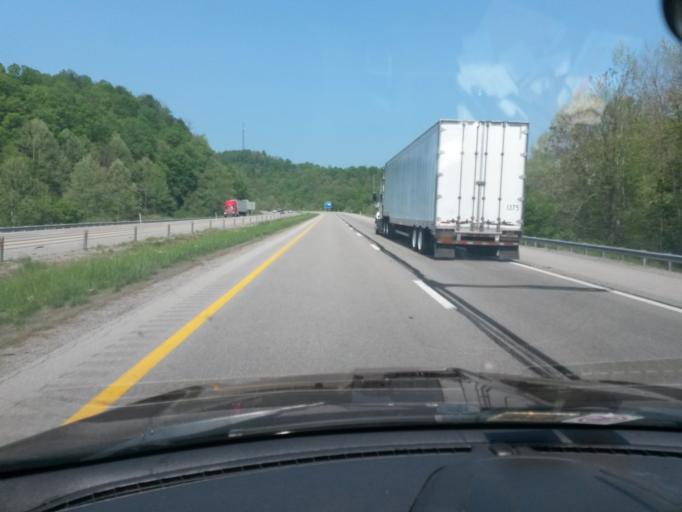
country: US
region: West Virginia
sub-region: Lewis County
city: Weston
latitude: 39.0170
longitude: -80.4383
